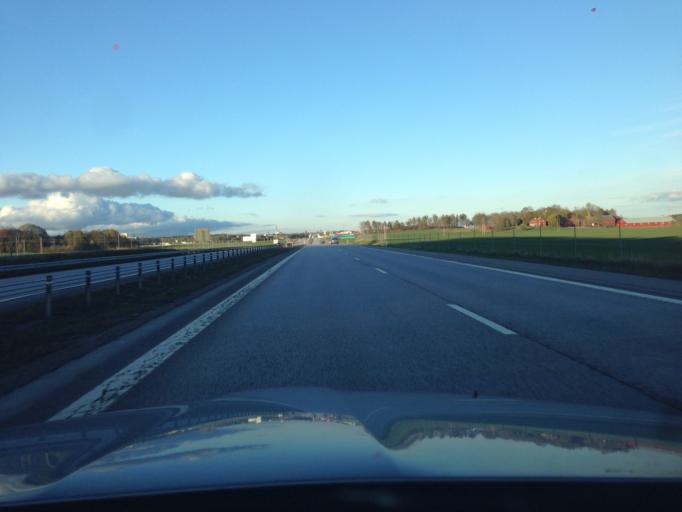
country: SE
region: Soedermanland
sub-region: Nykopings Kommun
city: Nykoping
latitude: 58.7463
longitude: 16.9516
